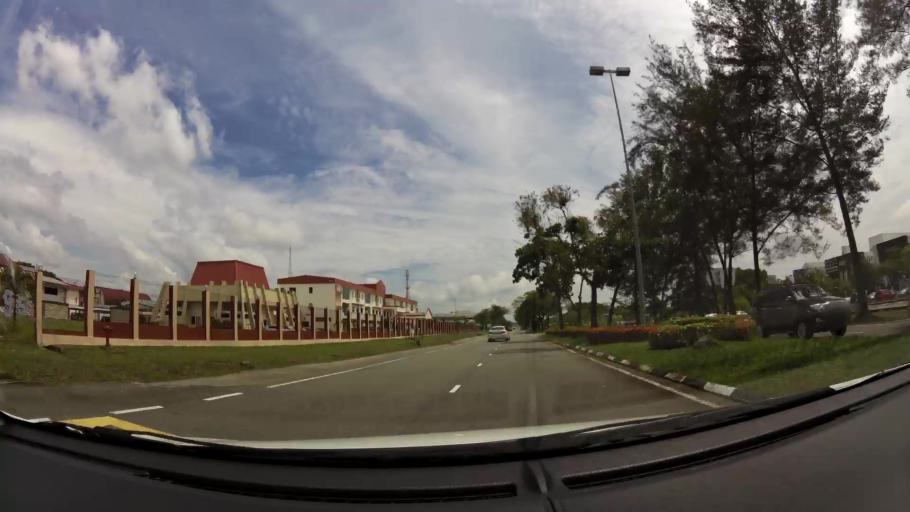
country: BN
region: Brunei and Muara
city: Bandar Seri Begawan
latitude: 4.9254
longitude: 114.9320
